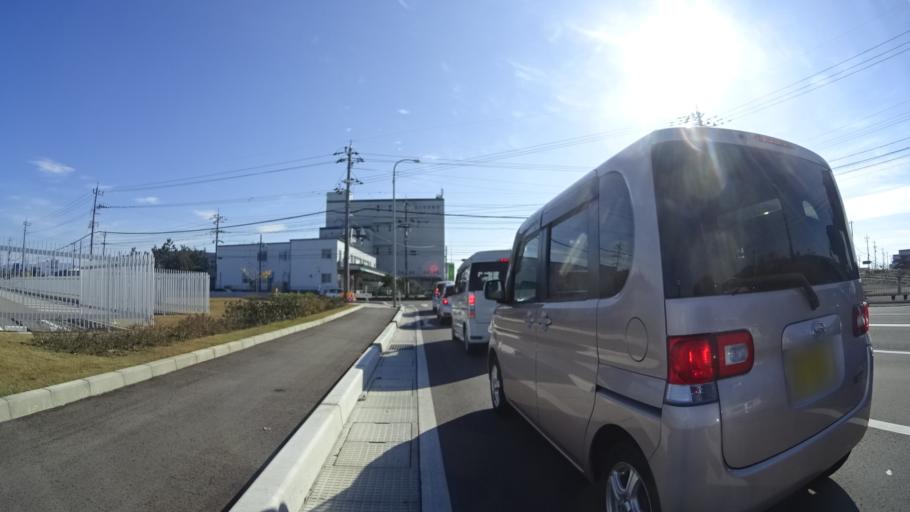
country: JP
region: Ishikawa
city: Kanazawa-shi
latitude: 36.6081
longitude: 136.6116
